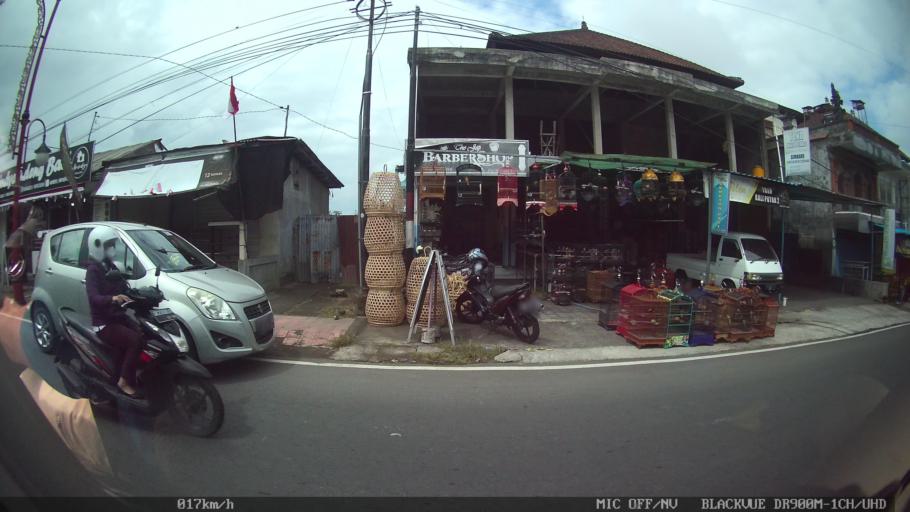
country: ID
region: Bali
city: Banjar Kelodan
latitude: -8.5358
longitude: 115.3296
